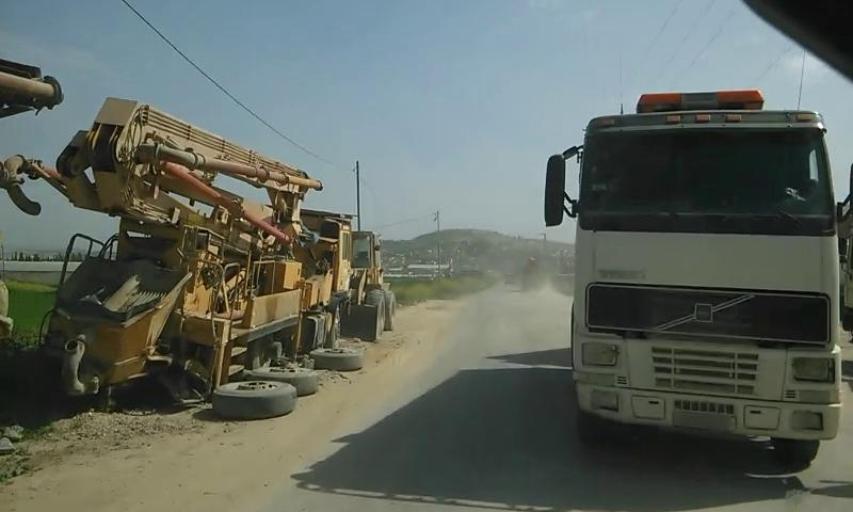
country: PS
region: West Bank
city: Ash Shuhada'
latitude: 32.4374
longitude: 35.2650
